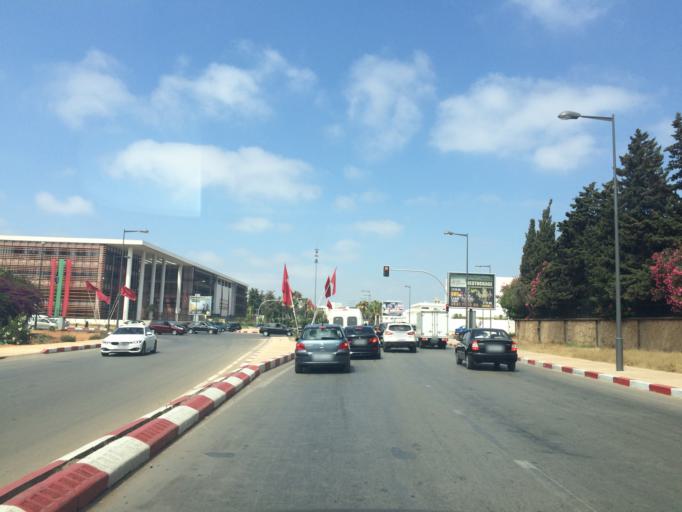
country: MA
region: Rabat-Sale-Zemmour-Zaer
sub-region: Skhirate-Temara
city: Temara
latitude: 33.9685
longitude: -6.8749
